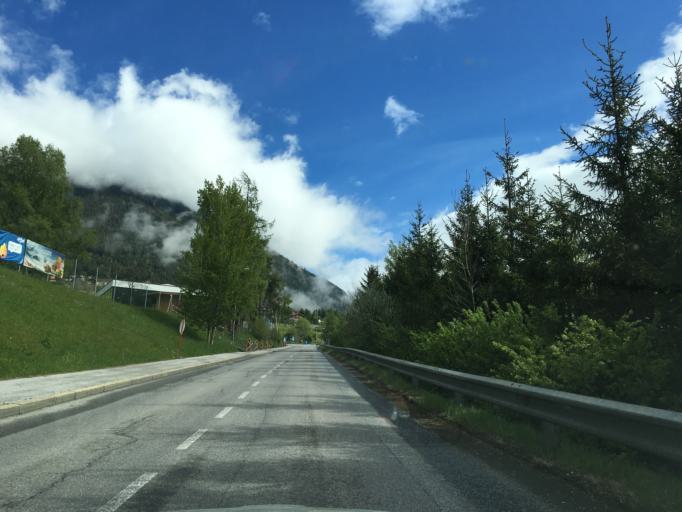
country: AT
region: Tyrol
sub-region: Politischer Bezirk Innsbruck Land
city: Fulpmes
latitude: 47.1588
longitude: 11.3551
